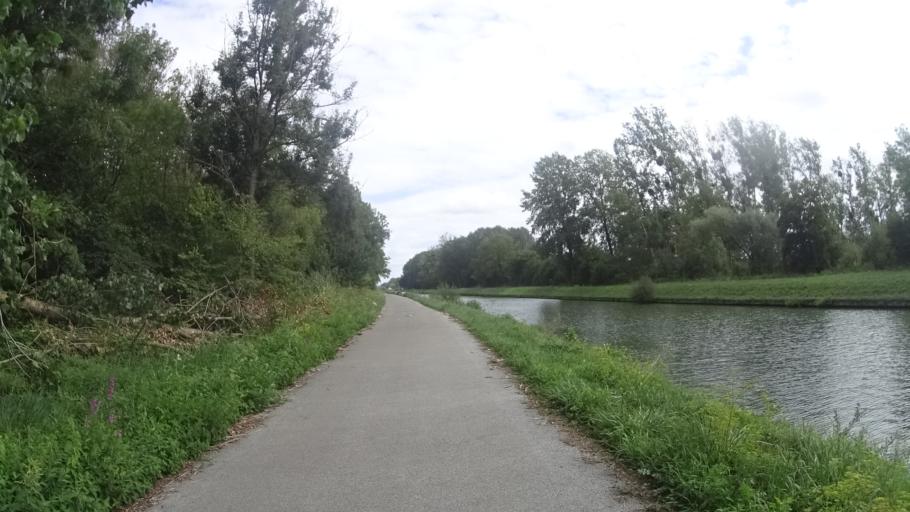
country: FR
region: Picardie
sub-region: Departement de l'Aisne
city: Blerancourt
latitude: 49.5771
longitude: 3.0974
